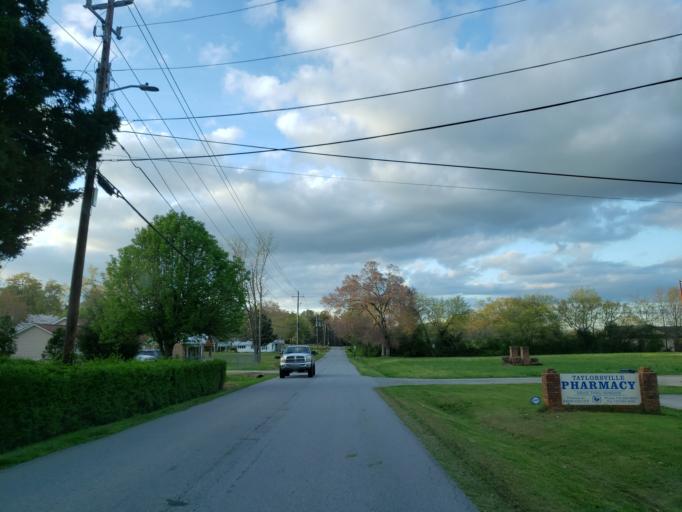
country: US
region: Georgia
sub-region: Polk County
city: Aragon
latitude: 34.0799
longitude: -84.9872
